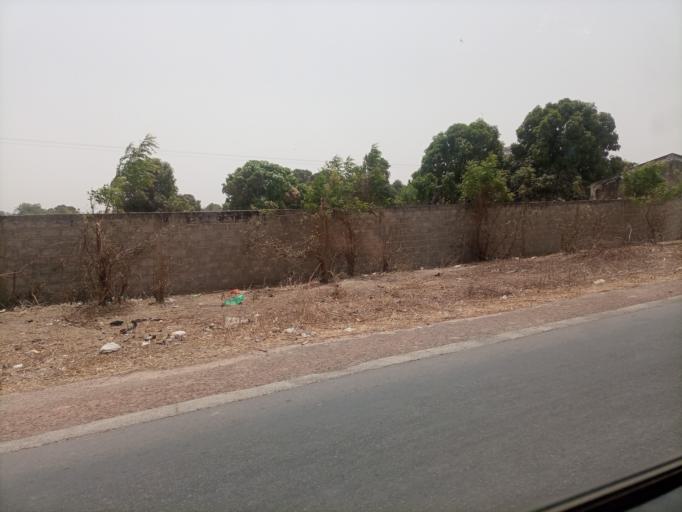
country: SN
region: Fatick
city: Sokone
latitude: 13.7021
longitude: -16.4299
